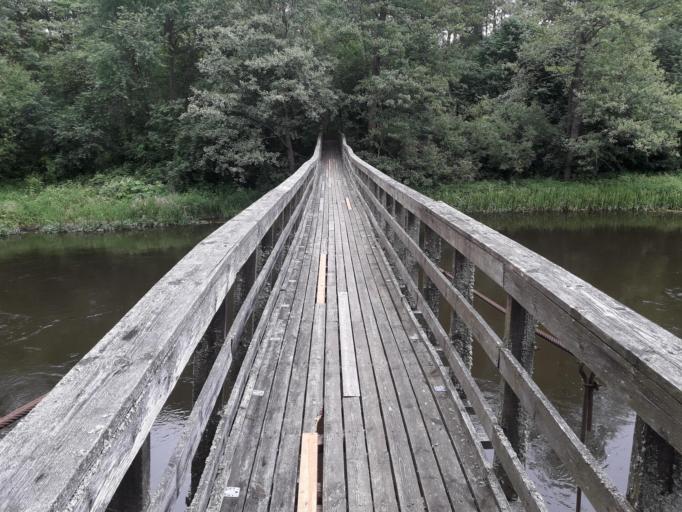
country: LT
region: Alytaus apskritis
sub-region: Alytaus rajonas
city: Daugai
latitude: 54.1170
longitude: 24.3029
